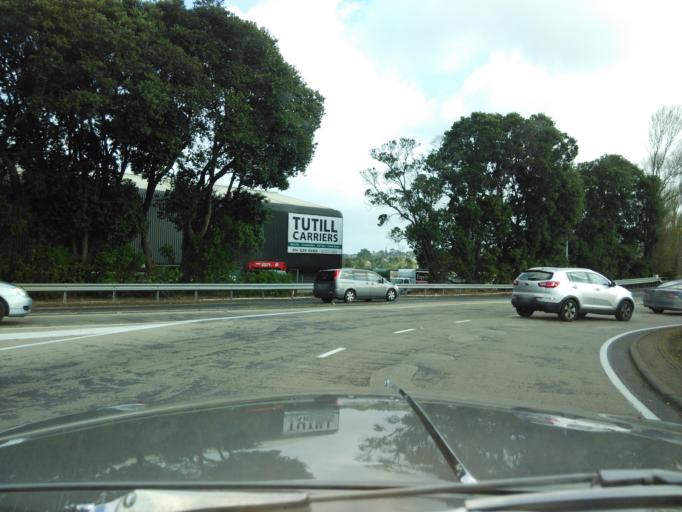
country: NZ
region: Auckland
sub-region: Auckland
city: Tamaki
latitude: -36.9042
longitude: 174.8117
